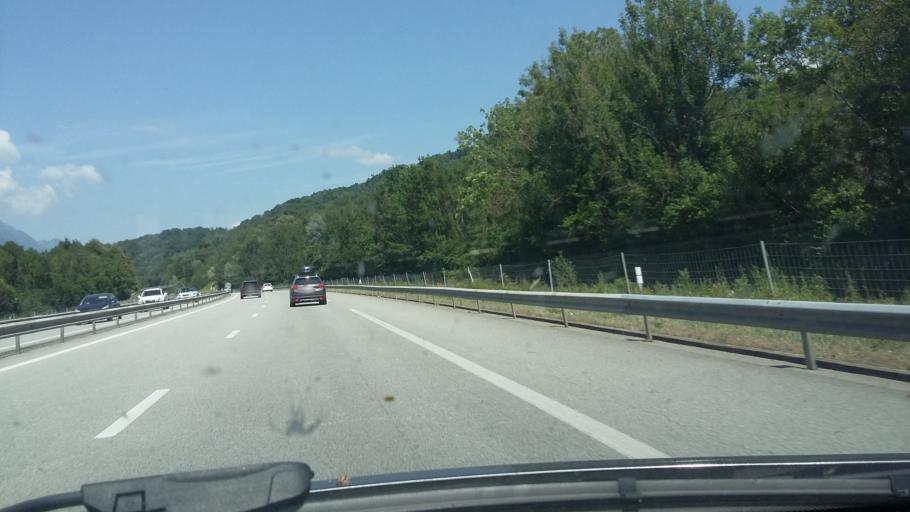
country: FR
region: Rhone-Alpes
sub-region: Departement de la Savoie
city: Cruet
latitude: 45.5091
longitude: 6.0967
